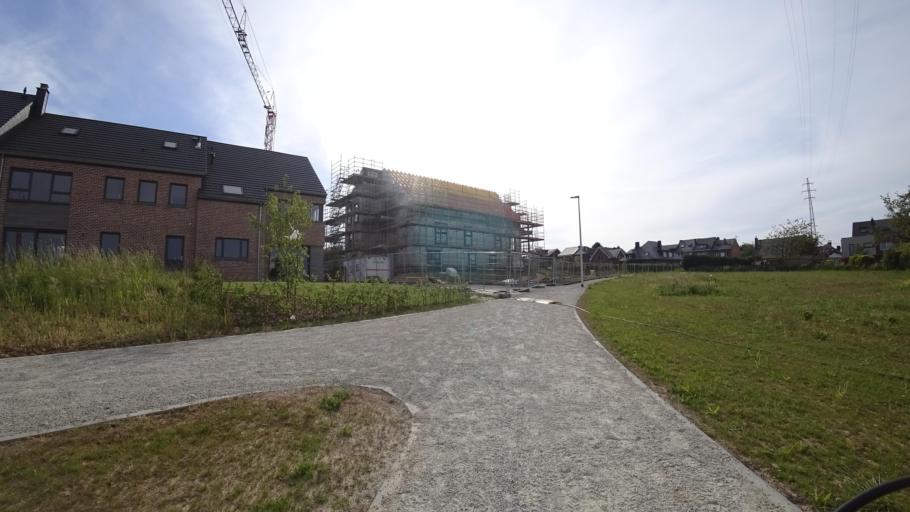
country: BE
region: Wallonia
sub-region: Province de Namur
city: Namur
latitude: 50.4656
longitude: 4.8284
